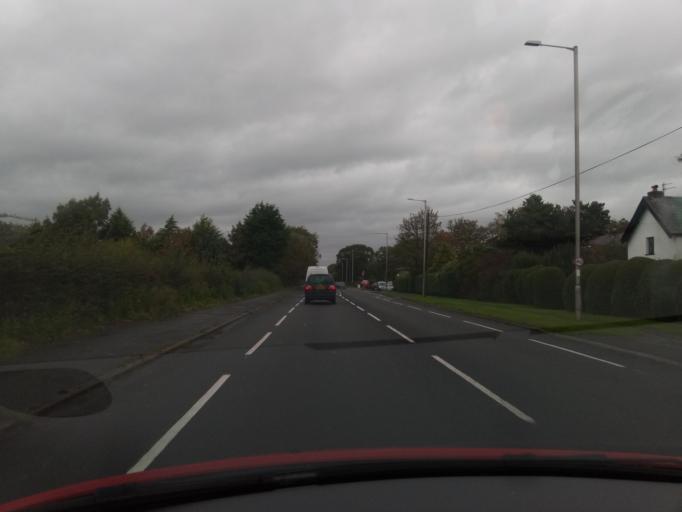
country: GB
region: England
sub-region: Lancashire
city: Catterall
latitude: 53.8256
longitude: -2.7361
